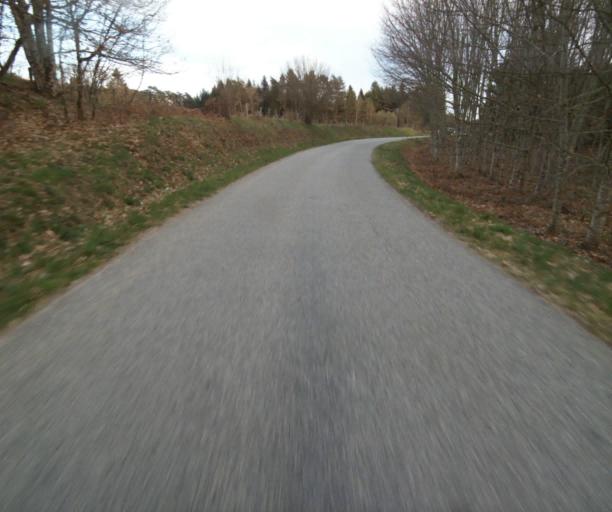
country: FR
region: Limousin
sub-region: Departement de la Correze
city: Correze
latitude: 45.2725
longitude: 1.9764
